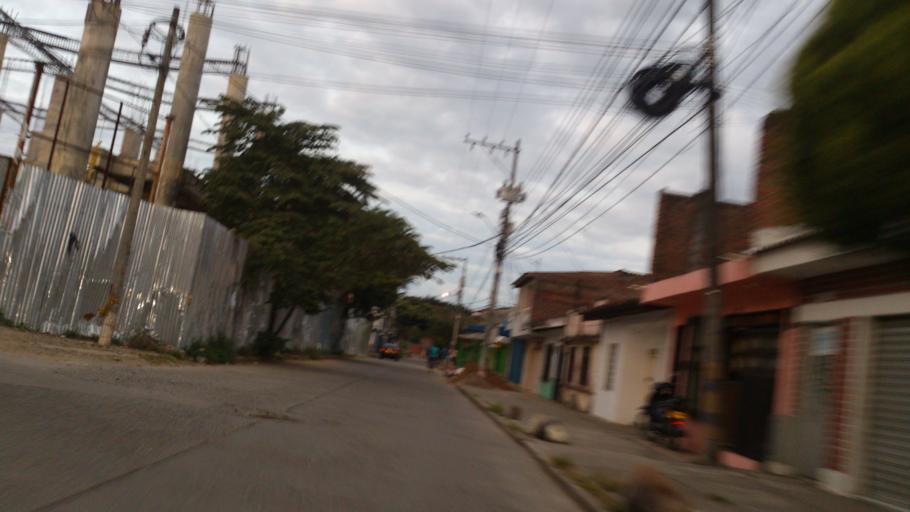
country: CO
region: Valle del Cauca
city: Jamundi
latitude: 3.2622
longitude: -76.5384
